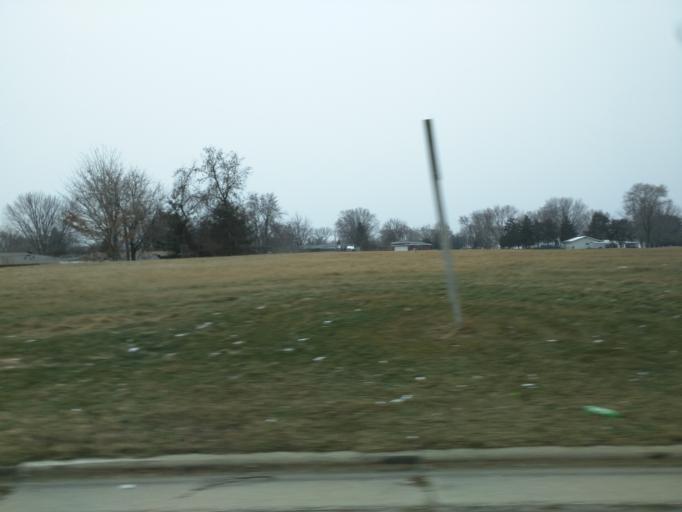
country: US
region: Wisconsin
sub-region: La Crosse County
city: French Island
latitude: 43.8656
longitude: -91.2619
